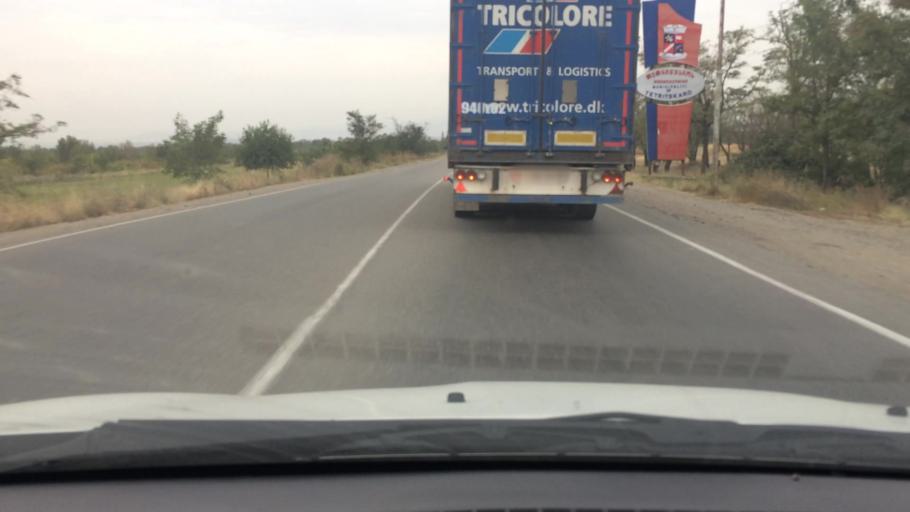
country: GE
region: T'bilisi
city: Tbilisi
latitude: 41.5910
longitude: 44.7802
